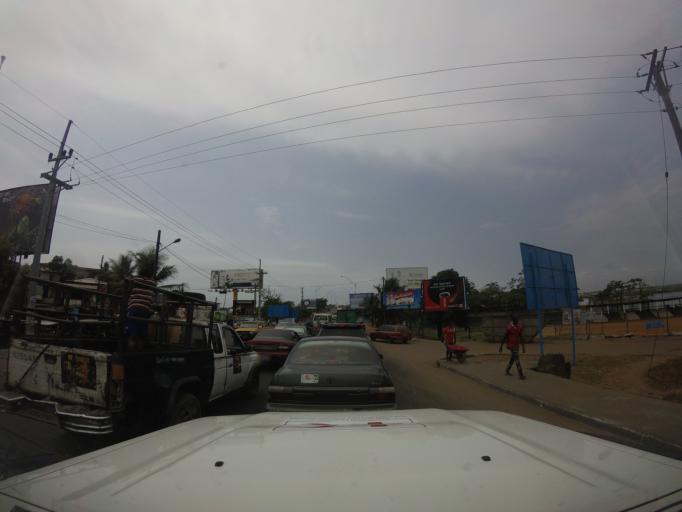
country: LR
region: Montserrado
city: Monrovia
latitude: 6.3174
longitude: -10.8015
